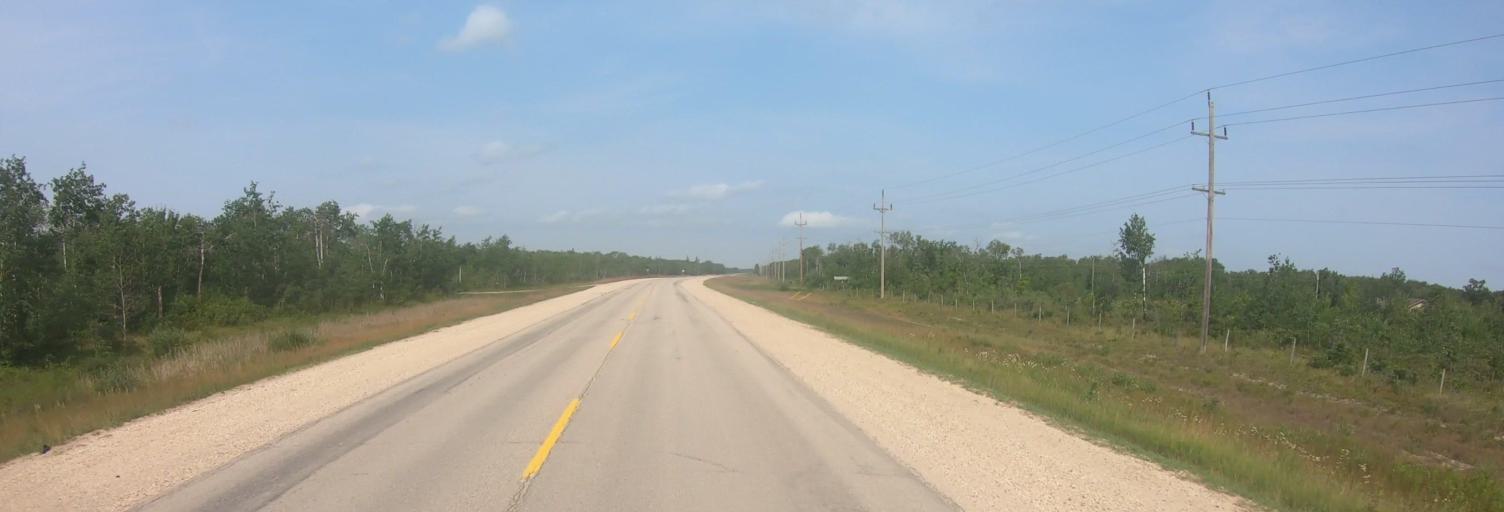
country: CA
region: Manitoba
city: Steinbach
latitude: 49.3566
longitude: -96.6638
